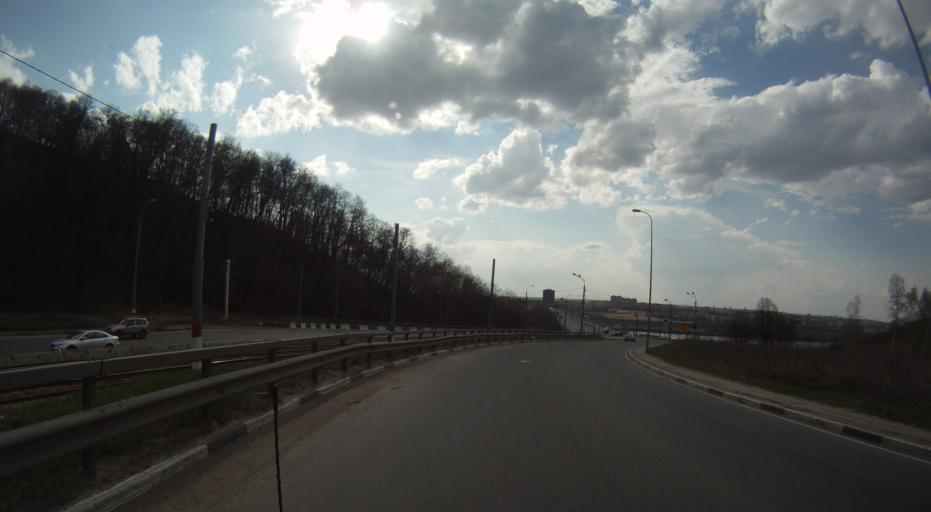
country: RU
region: Nizjnij Novgorod
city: Nizhniy Novgorod
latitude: 56.2986
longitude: 43.9723
